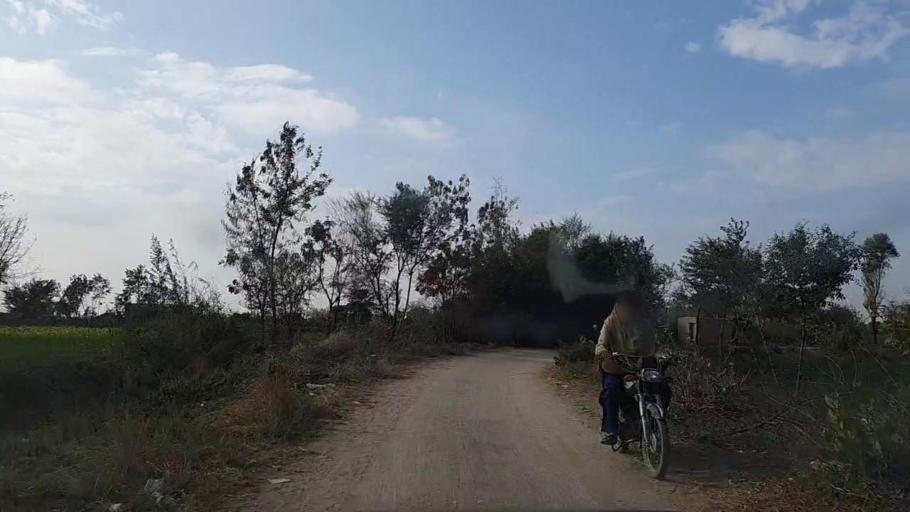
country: PK
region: Sindh
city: Sanghar
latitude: 26.2442
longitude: 69.0173
